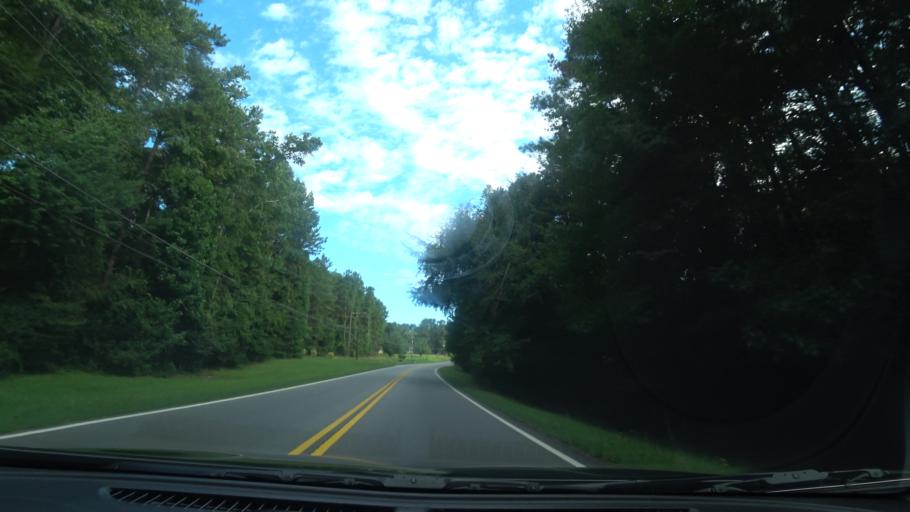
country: US
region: Georgia
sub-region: Rockdale County
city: Lakeview Estates
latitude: 33.7168
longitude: -84.0061
